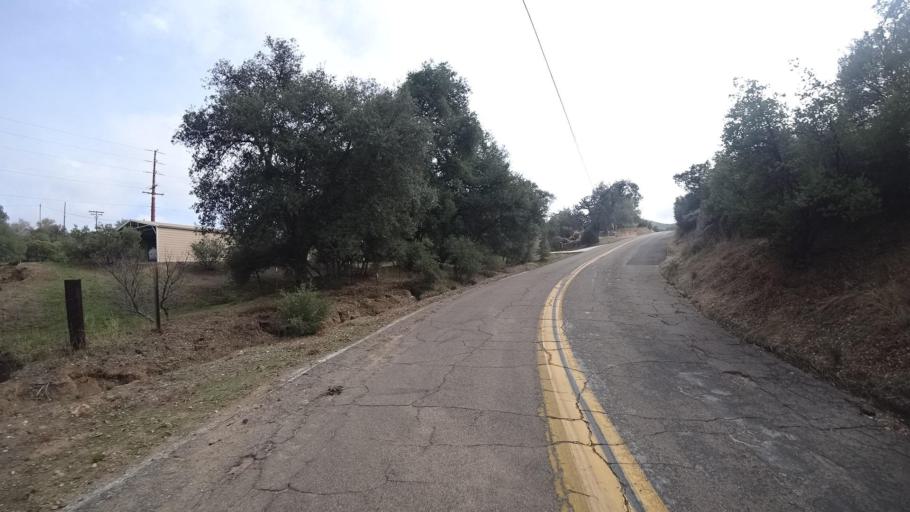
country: US
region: California
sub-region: San Diego County
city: Descanso
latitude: 32.8644
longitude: -116.6344
